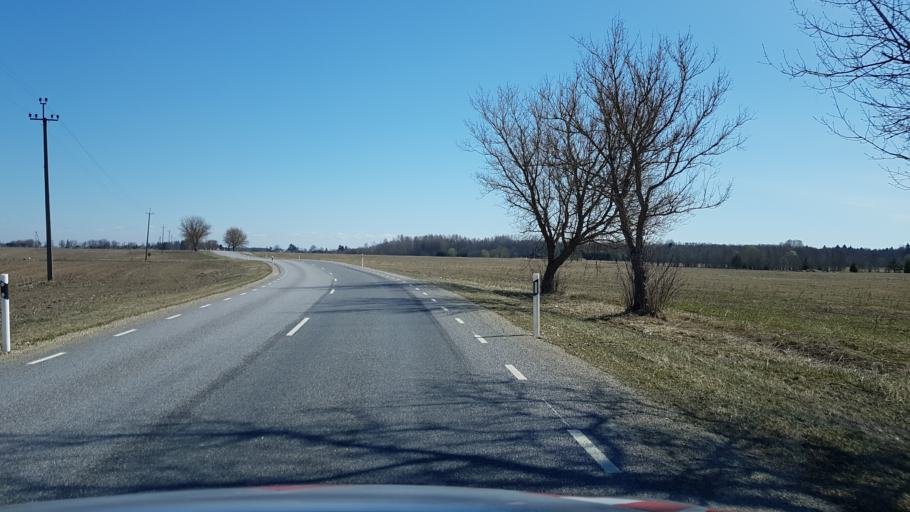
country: EE
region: Ida-Virumaa
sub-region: Kohtla-Jaerve linn
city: Kohtla-Jarve
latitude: 59.3359
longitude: 27.3120
